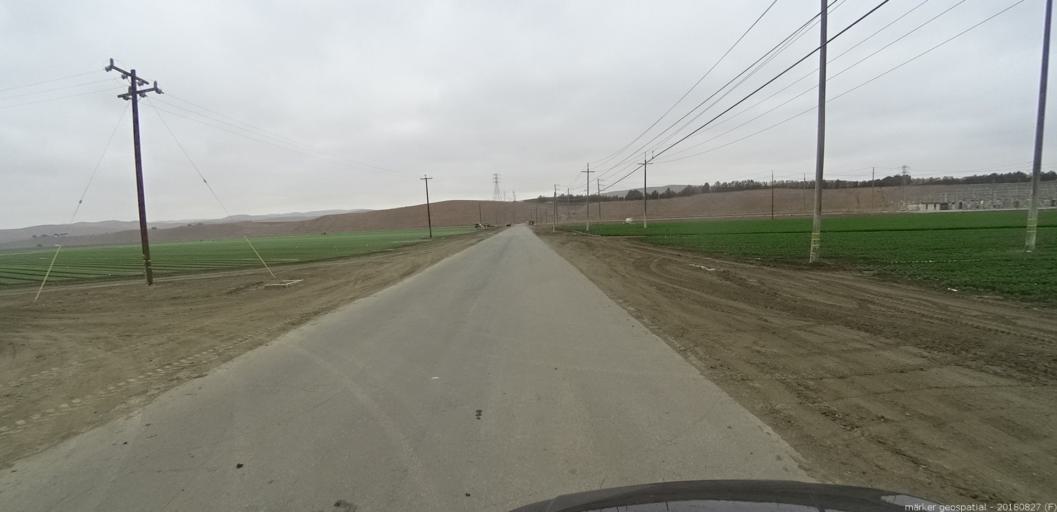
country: US
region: California
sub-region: Monterey County
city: King City
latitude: 36.2653
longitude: -121.1496
